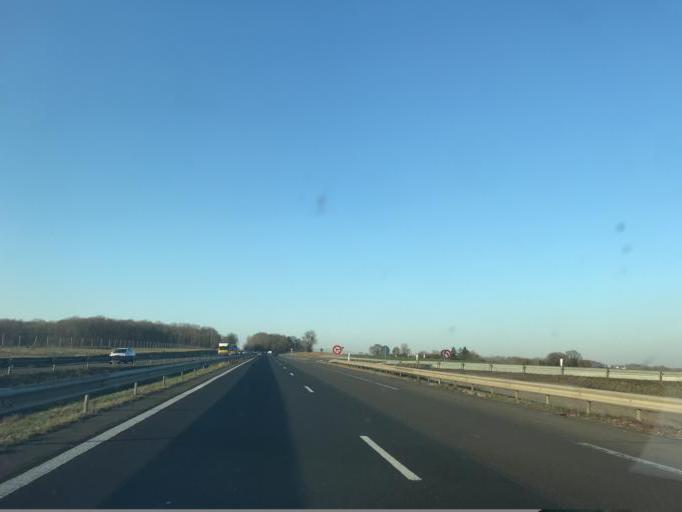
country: FR
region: Ile-de-France
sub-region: Departement de Seine-et-Marne
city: Bouleurs
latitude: 48.8880
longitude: 2.8957
